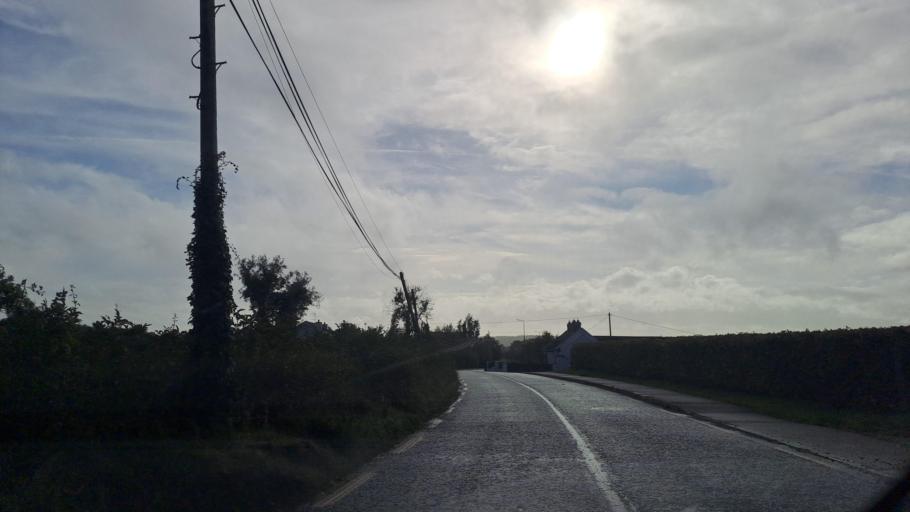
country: IE
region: Ulster
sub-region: County Monaghan
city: Carrickmacross
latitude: 53.9360
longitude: -6.7165
